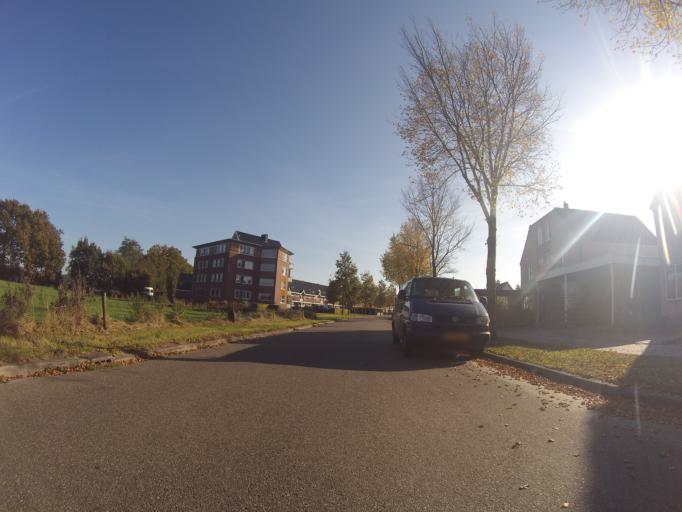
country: NL
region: Gelderland
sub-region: Gemeente Barneveld
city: Terschuur
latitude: 52.1378
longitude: 5.4989
